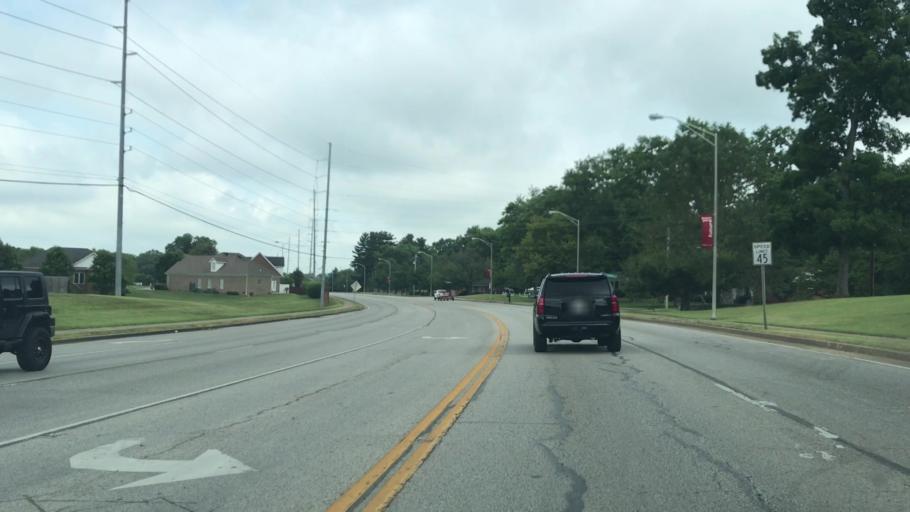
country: US
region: Kentucky
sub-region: Warren County
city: Bowling Green
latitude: 36.9879
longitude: -86.4046
